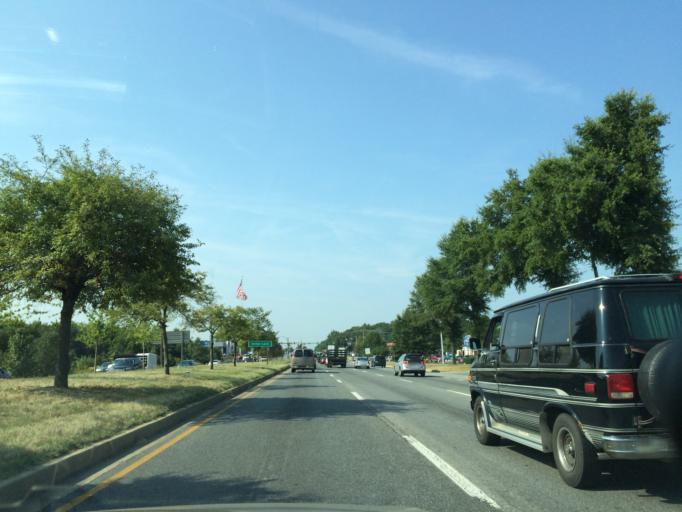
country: US
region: Maryland
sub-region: Charles County
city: Waldorf
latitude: 38.6413
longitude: -76.8955
